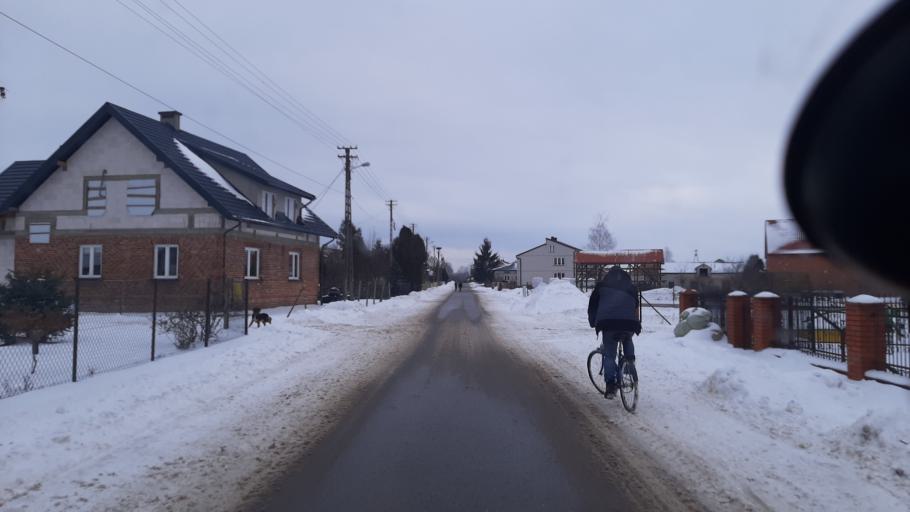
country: PL
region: Lublin Voivodeship
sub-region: Powiat lubartowski
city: Abramow
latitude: 51.4407
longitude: 22.2950
